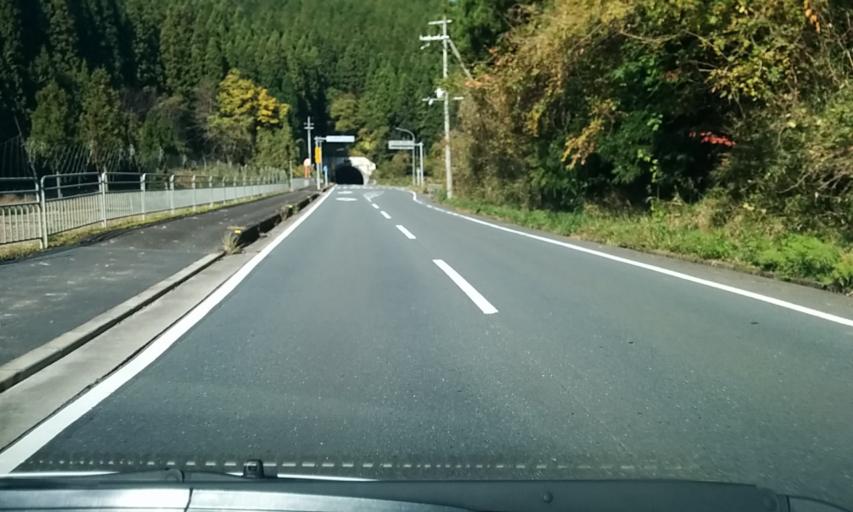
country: JP
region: Kyoto
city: Kameoka
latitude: 35.1606
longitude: 135.5149
